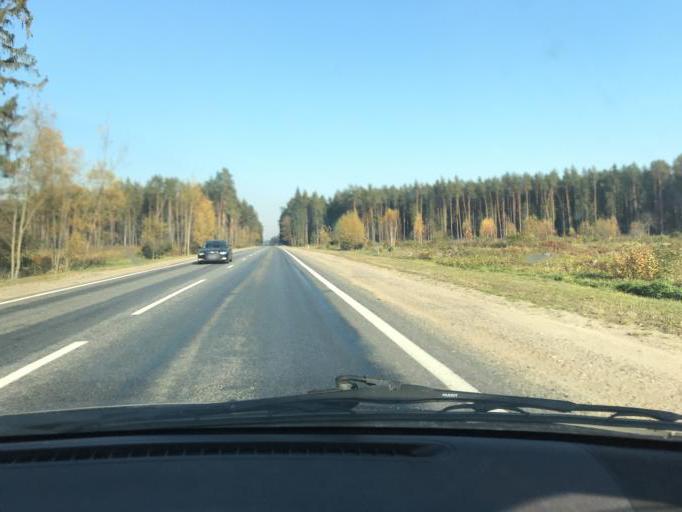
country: BY
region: Vitebsk
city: Orsha
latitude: 54.4079
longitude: 30.4508
